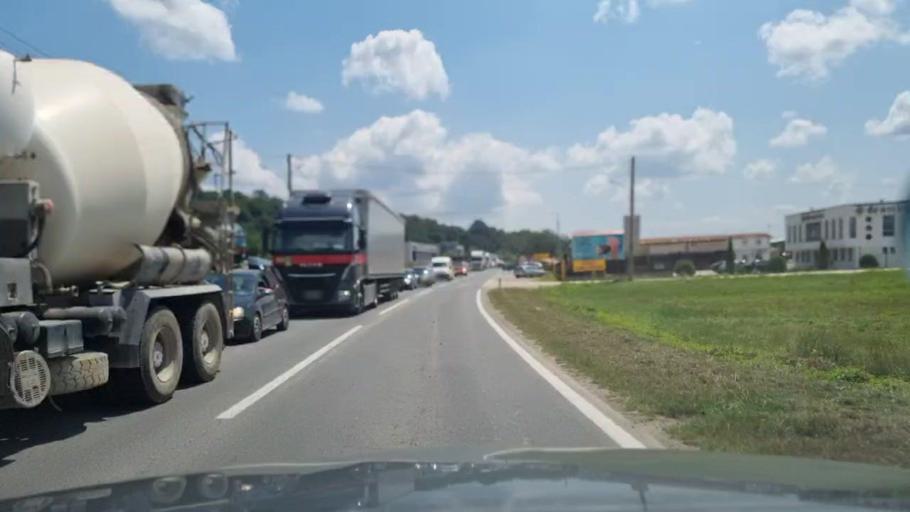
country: BA
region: Federation of Bosnia and Herzegovina
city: Orahovica Donja
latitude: 44.6606
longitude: 18.3413
